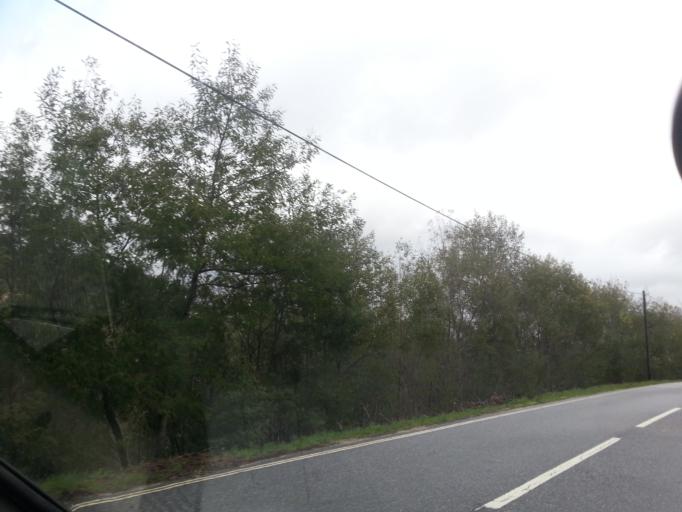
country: PT
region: Guarda
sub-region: Fornos de Algodres
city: Fornos de Algodres
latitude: 40.6179
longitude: -7.4982
